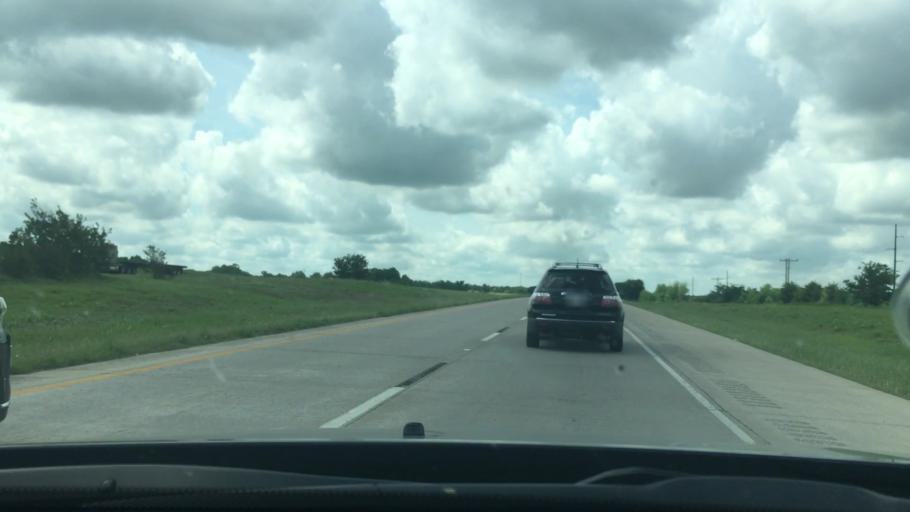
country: US
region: Oklahoma
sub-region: Love County
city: Marietta
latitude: 33.8689
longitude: -97.1344
